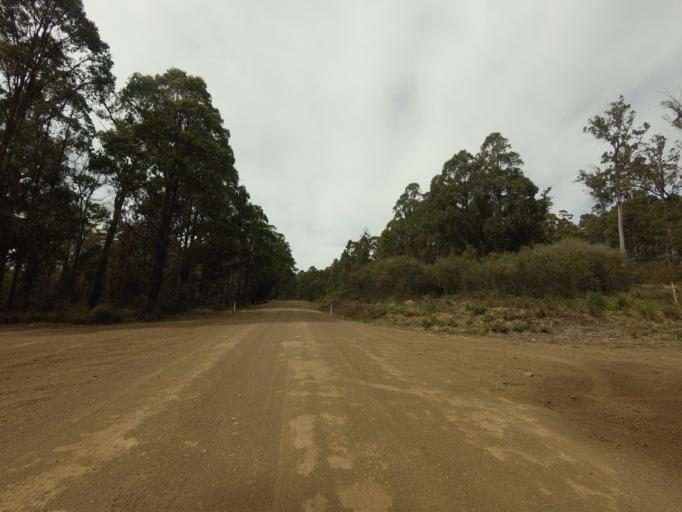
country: AU
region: Tasmania
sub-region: Sorell
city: Sorell
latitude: -42.4857
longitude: 147.6172
